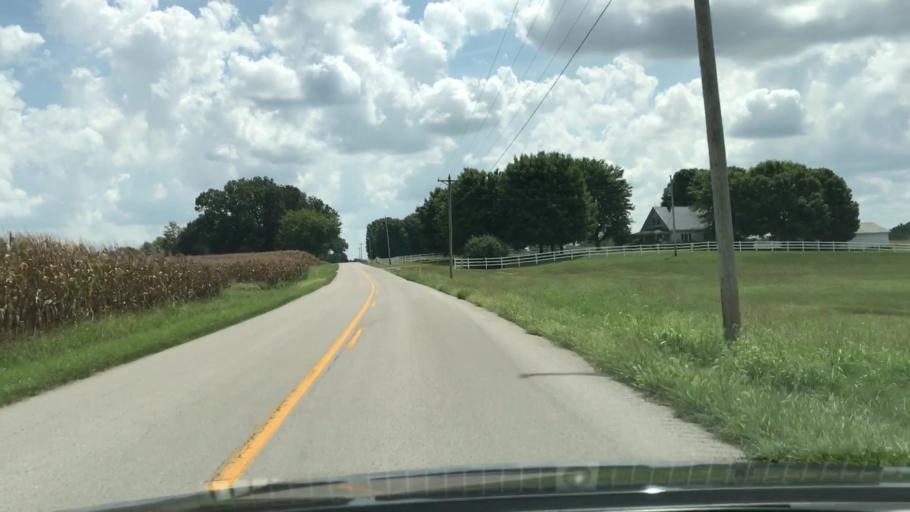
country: US
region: Kentucky
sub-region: Todd County
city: Elkton
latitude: 36.7886
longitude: -87.1346
